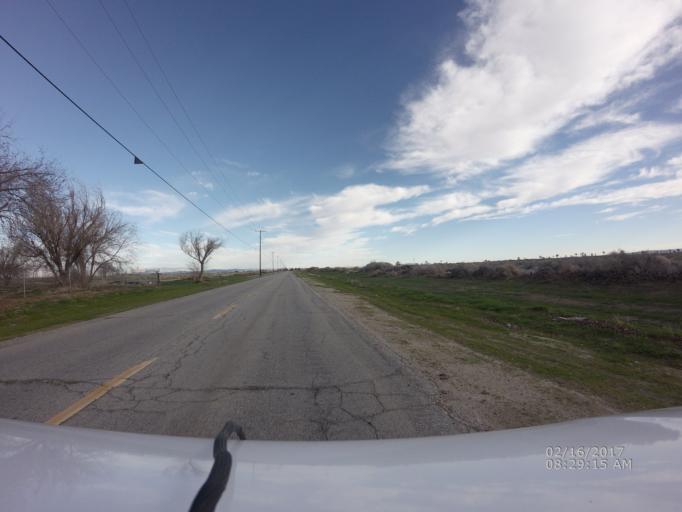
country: US
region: California
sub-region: Los Angeles County
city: Lancaster
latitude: 34.6944
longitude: -118.0054
